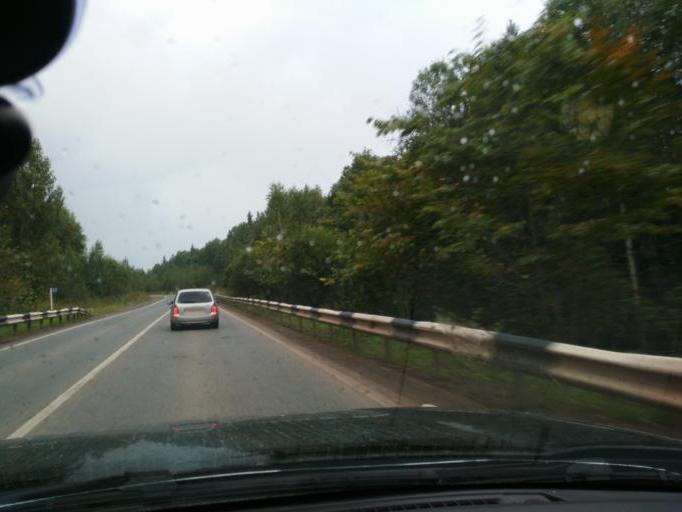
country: RU
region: Perm
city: Barda
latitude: 56.8918
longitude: 55.7766
